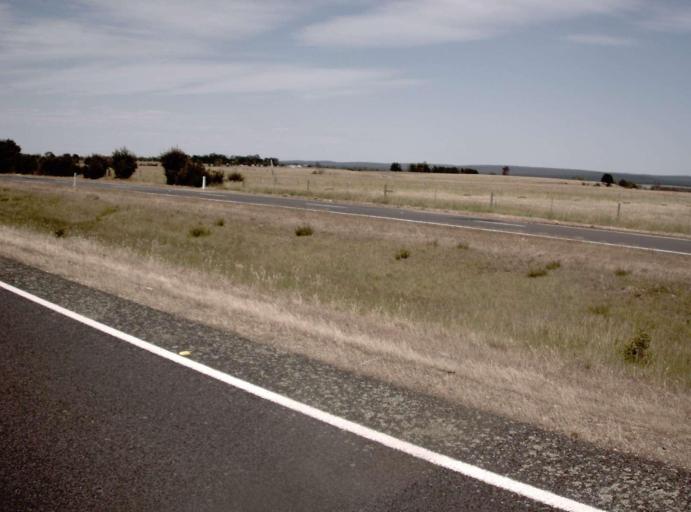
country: AU
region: Victoria
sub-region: Wellington
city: Heyfield
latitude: -38.1355
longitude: 146.8004
